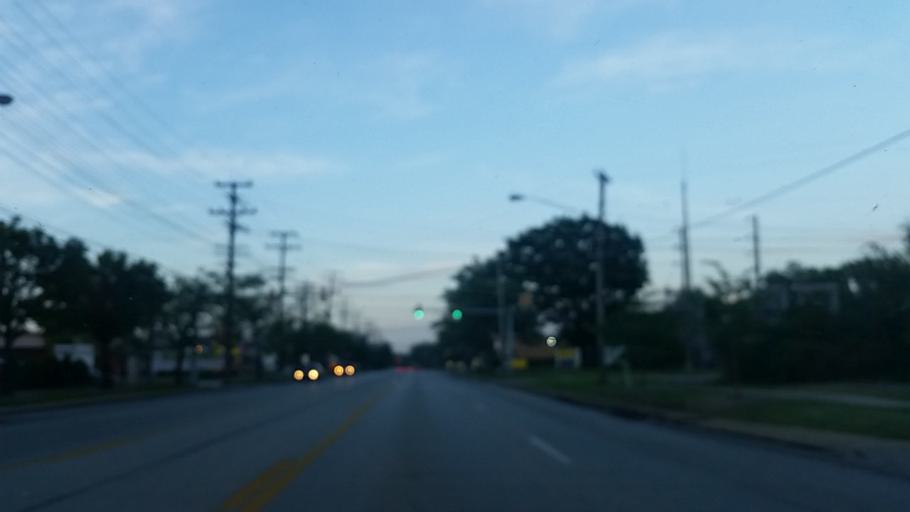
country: US
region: Ohio
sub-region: Cuyahoga County
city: Parma Heights
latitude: 41.3837
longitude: -81.7754
